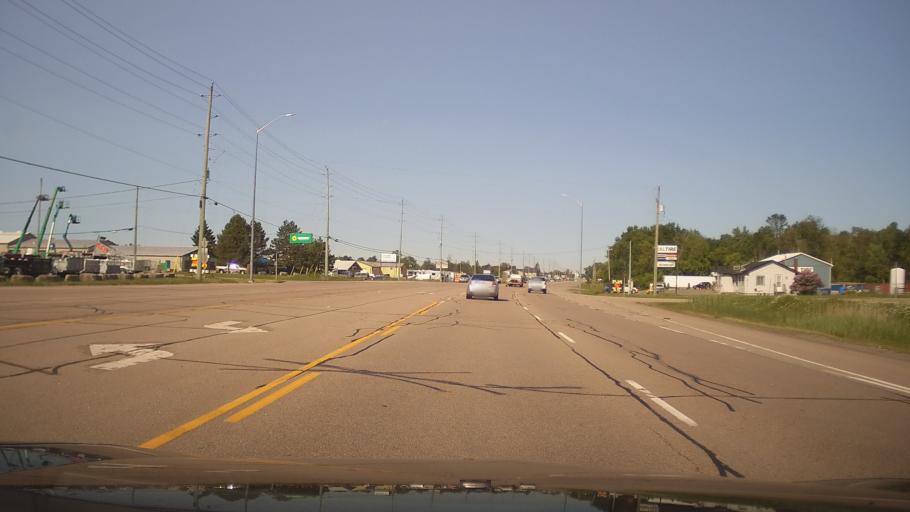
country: CA
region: Ontario
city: Peterborough
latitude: 44.3028
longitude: -78.2465
